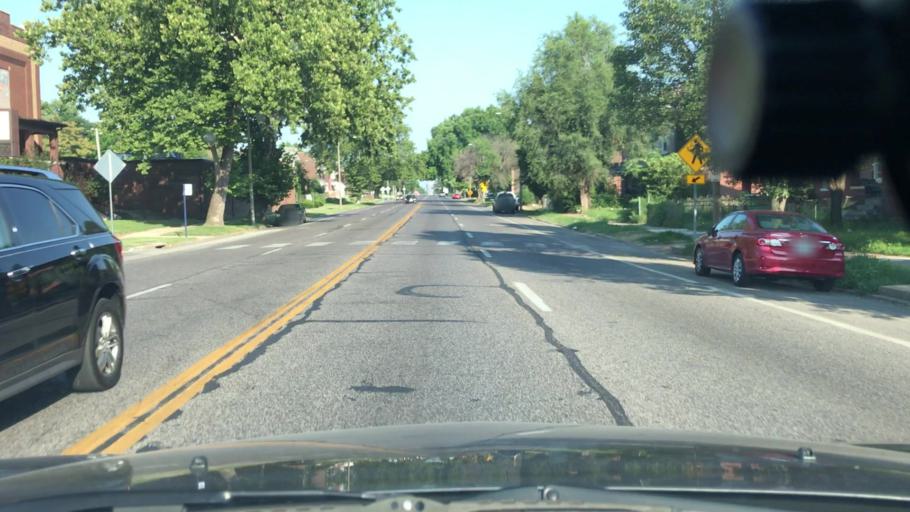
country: US
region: Missouri
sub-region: Saint Louis County
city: Hillsdale
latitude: 38.6581
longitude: -90.2552
